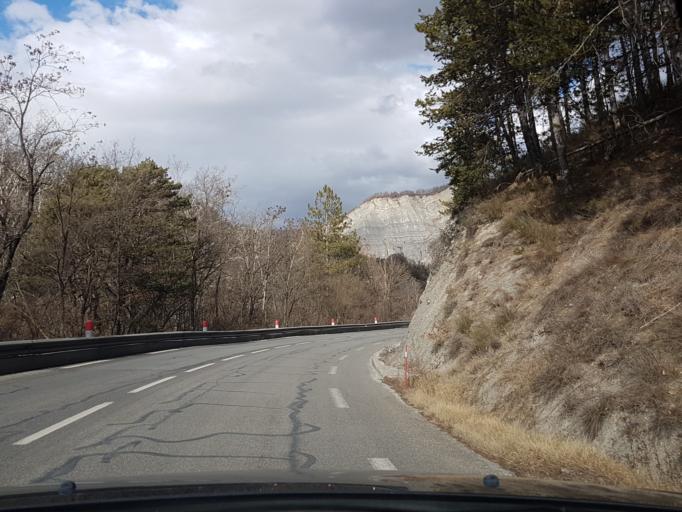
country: FR
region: Provence-Alpes-Cote d'Azur
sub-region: Departement des Hautes-Alpes
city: Tallard
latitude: 44.5027
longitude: 6.0811
